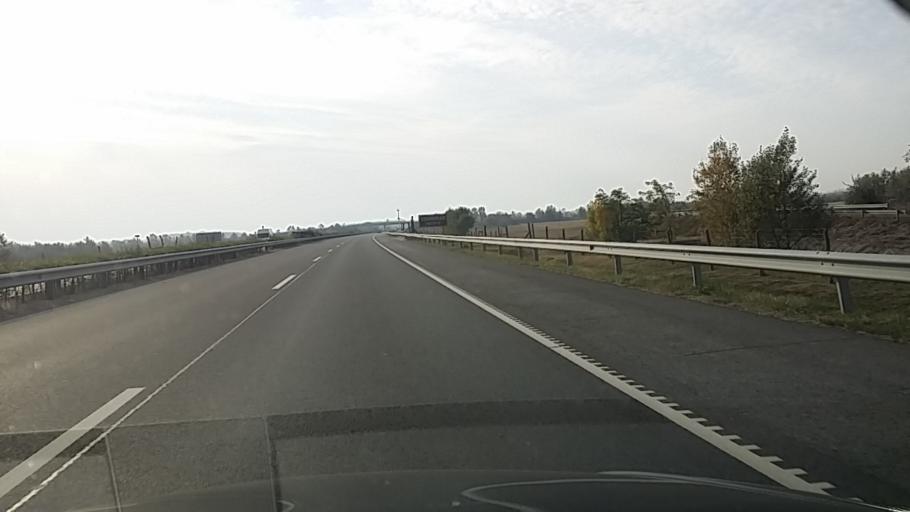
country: HU
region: Csongrad
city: Csengele
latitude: 46.5732
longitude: 19.8739
